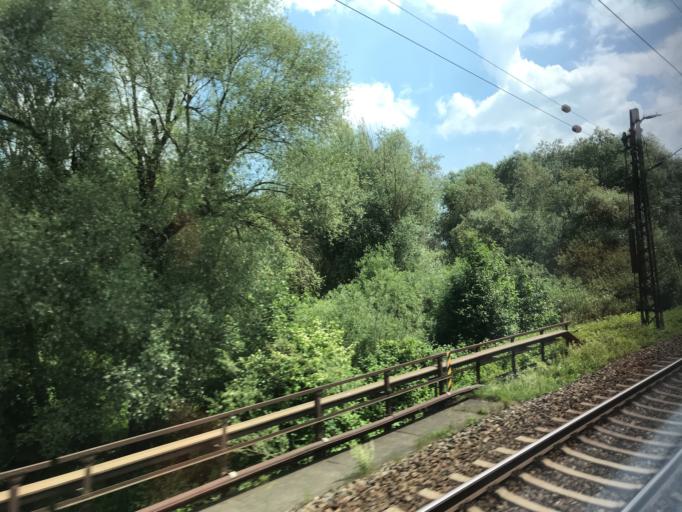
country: DE
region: Bavaria
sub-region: Swabia
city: Offingen
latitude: 48.4864
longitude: 10.3687
